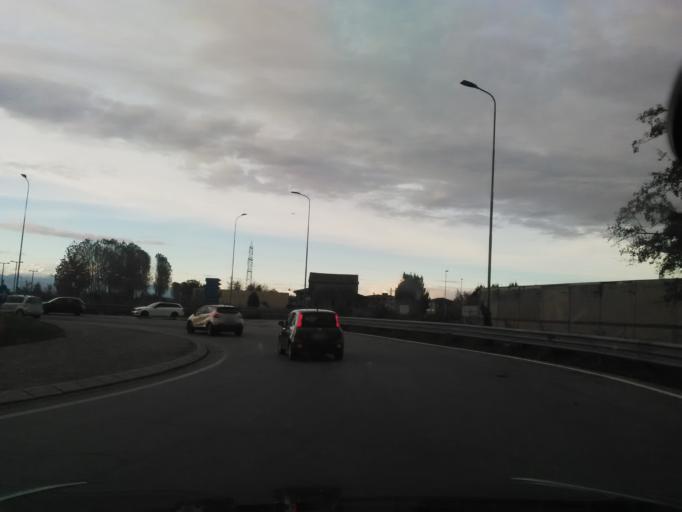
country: IT
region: Piedmont
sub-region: Provincia di Novara
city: Vicolungo
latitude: 45.4693
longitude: 8.4656
